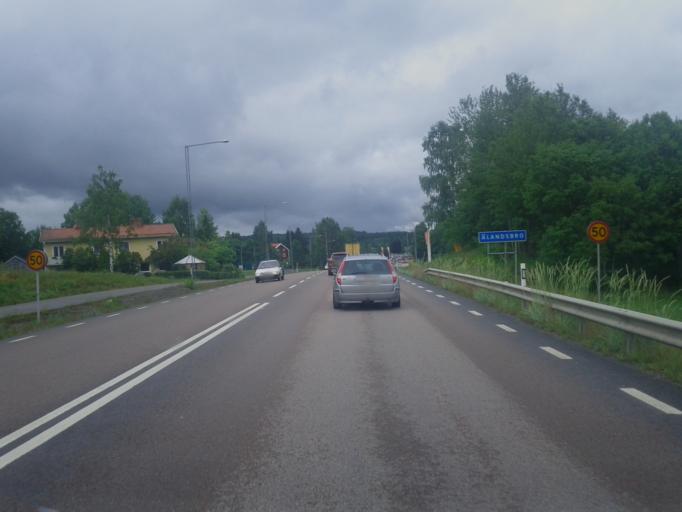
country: SE
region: Vaesternorrland
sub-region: Haernoesands Kommun
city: Haernoesand
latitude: 62.6698
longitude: 17.8407
